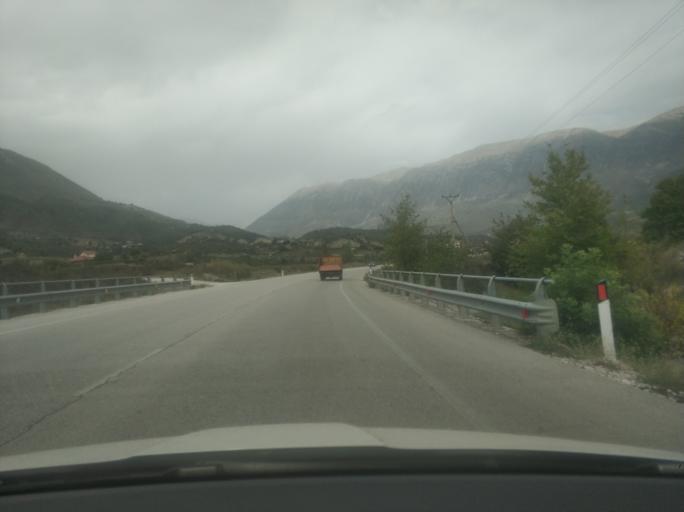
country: AL
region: Gjirokaster
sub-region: Rrethi i Gjirokastres
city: Picar
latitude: 40.1832
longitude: 20.0763
